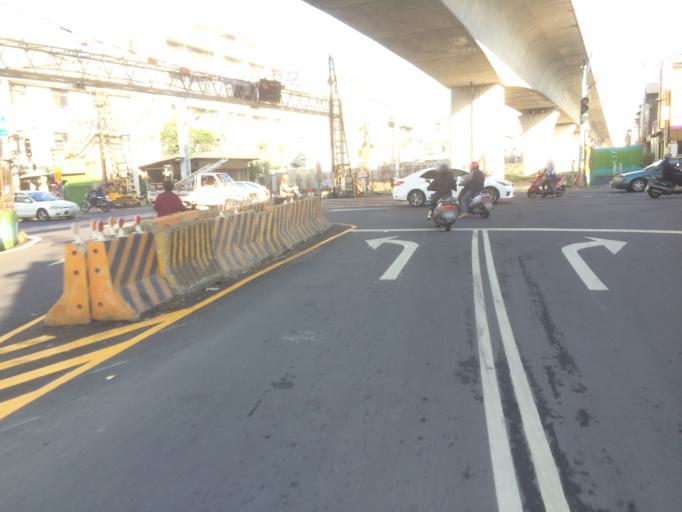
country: TW
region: Taiwan
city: Fengyuan
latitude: 24.2153
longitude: 120.7062
